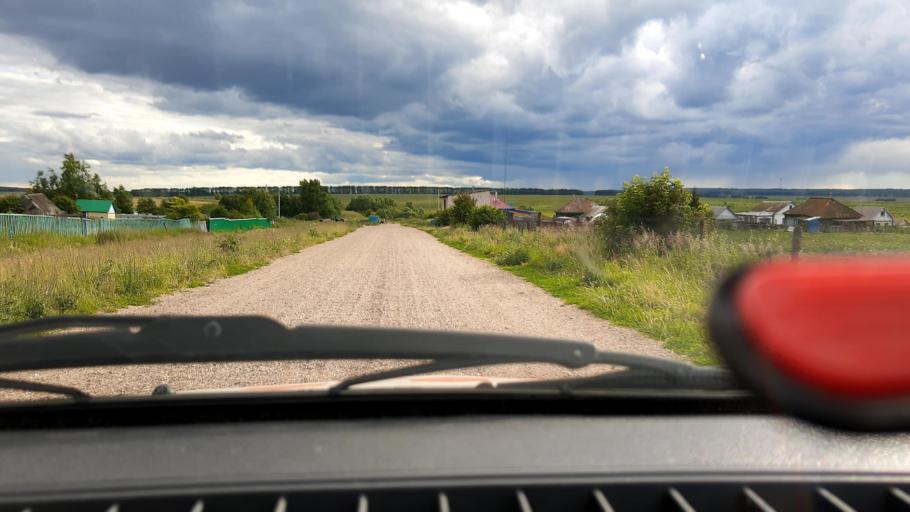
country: RU
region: Bashkortostan
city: Karmaskaly
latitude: 54.4223
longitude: 56.0244
